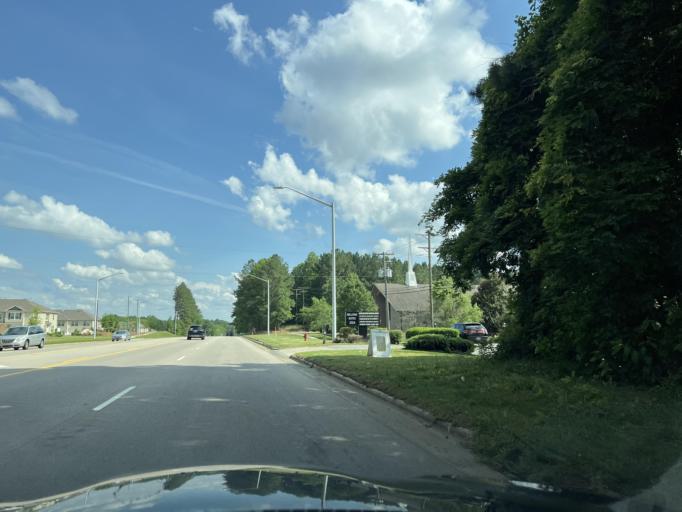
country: US
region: North Carolina
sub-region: Durham County
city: Durham
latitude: 35.9544
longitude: -78.8911
